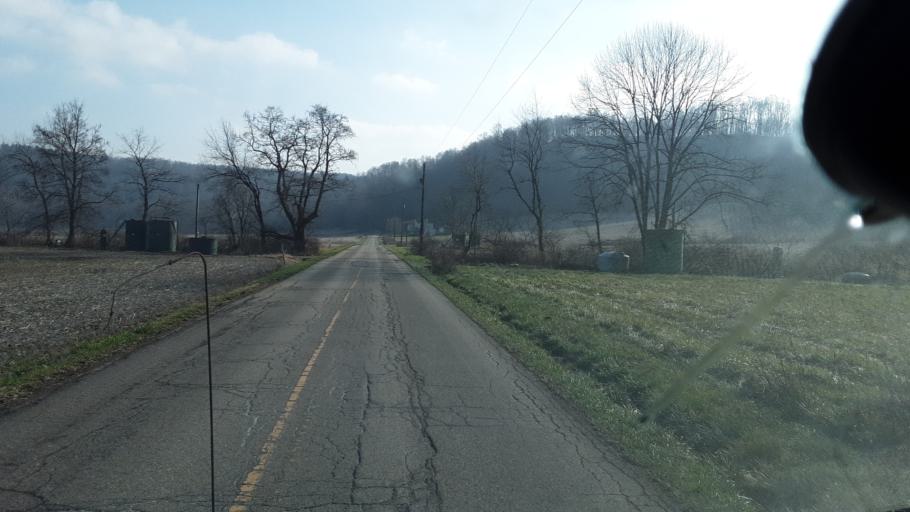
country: US
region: Ohio
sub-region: Knox County
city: Oak Hill
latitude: 40.4303
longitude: -82.2025
